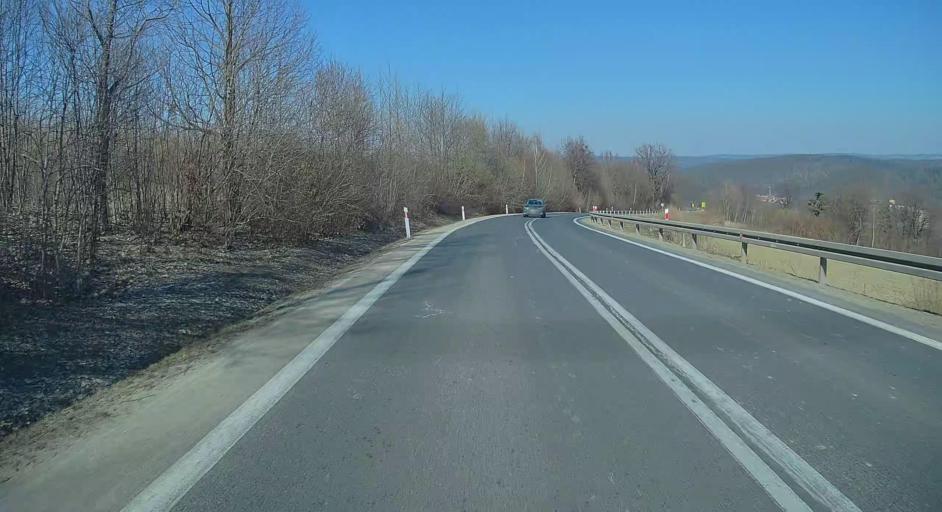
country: PL
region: Subcarpathian Voivodeship
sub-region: Powiat przemyski
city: Bircza
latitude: 49.6497
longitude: 22.4209
